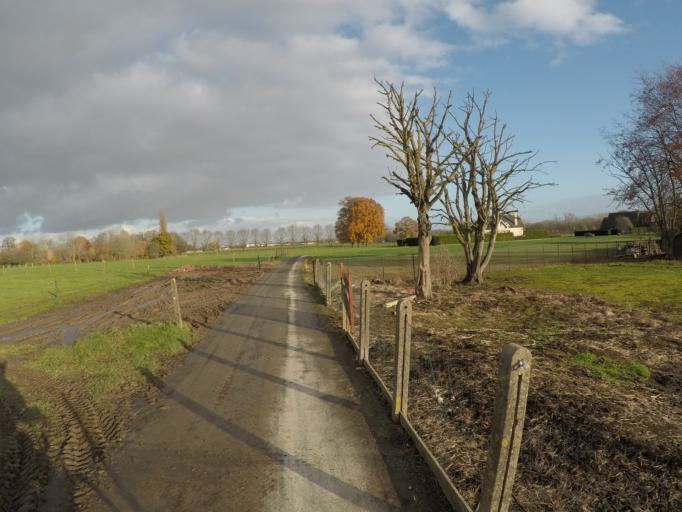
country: BE
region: Flanders
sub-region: Provincie Vlaams-Brabant
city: Opwijk
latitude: 50.9565
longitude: 4.1851
